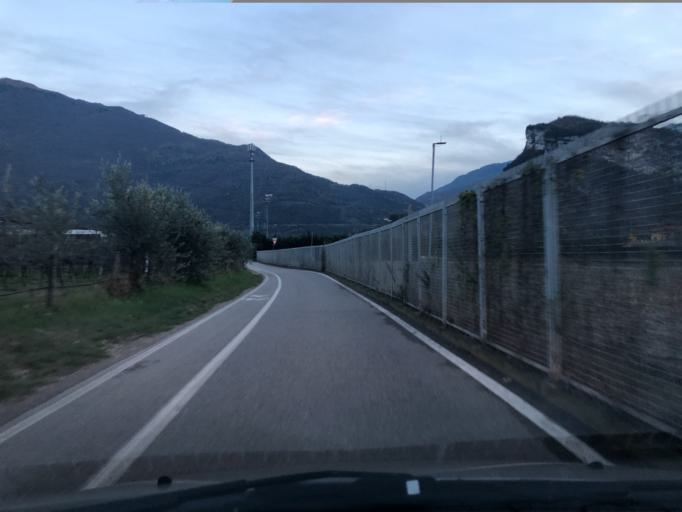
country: IT
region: Trentino-Alto Adige
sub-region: Provincia di Trento
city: Arco
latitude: 45.9023
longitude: 10.8683
